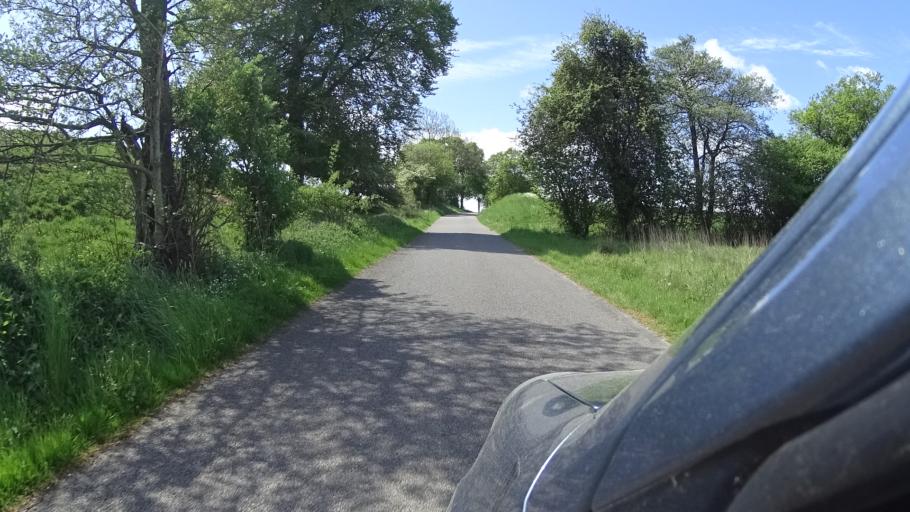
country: DK
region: South Denmark
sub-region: Vejle Kommune
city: Borkop
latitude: 55.6155
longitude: 9.6574
